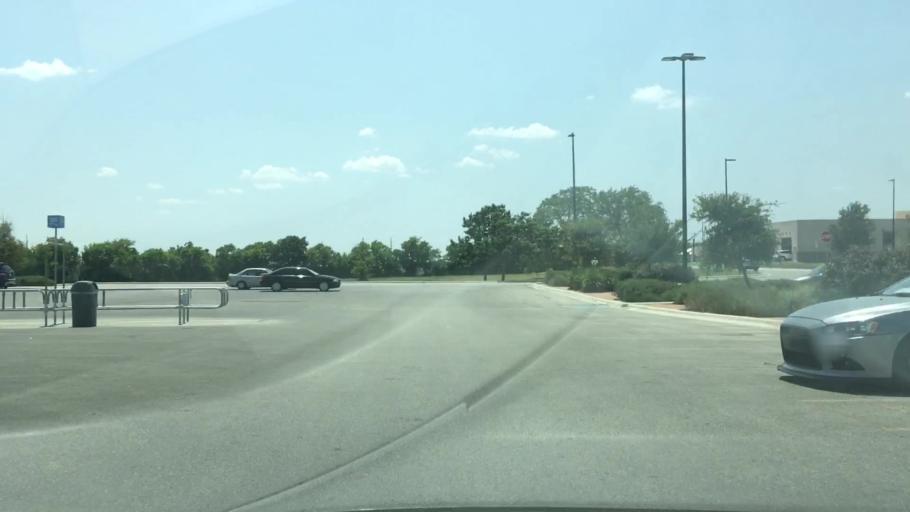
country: US
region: Texas
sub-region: Guadalupe County
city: Cibolo
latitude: 29.5730
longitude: -98.2374
